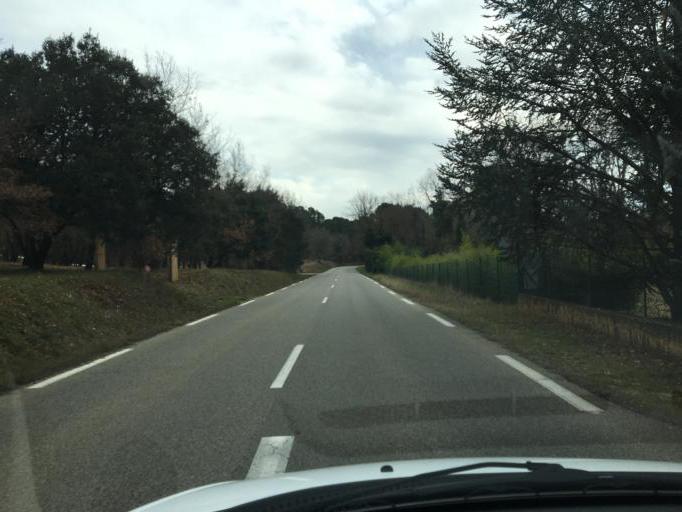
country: FR
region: Provence-Alpes-Cote d'Azur
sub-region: Departement du Vaucluse
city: Mormoiron
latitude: 44.0560
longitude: 5.1946
